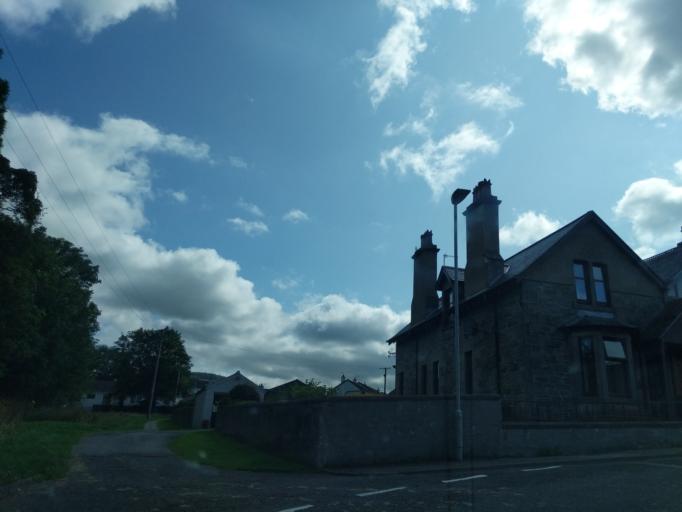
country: GB
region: Scotland
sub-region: Moray
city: Rothes
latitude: 57.4876
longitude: -3.1820
